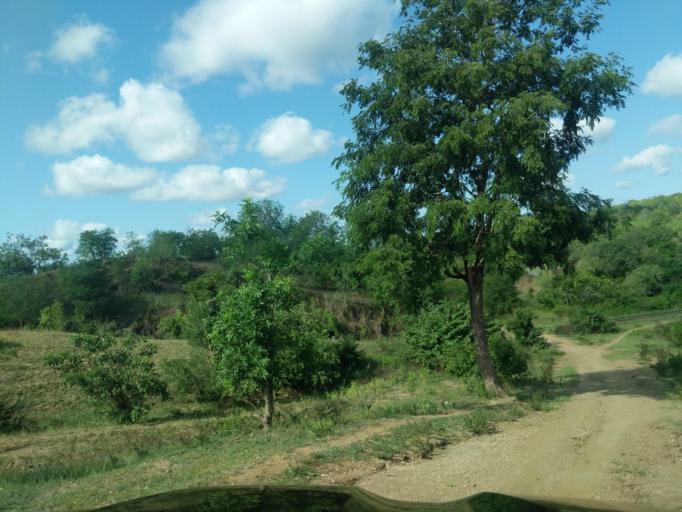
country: TZ
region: Tanga
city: Muheza
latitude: -5.4234
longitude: 38.6486
